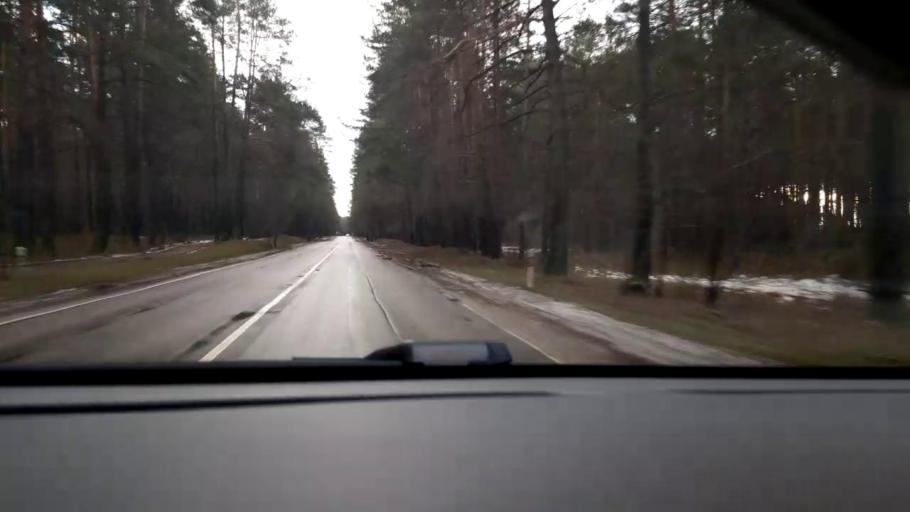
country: LT
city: Nemencine
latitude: 54.7811
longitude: 25.3838
